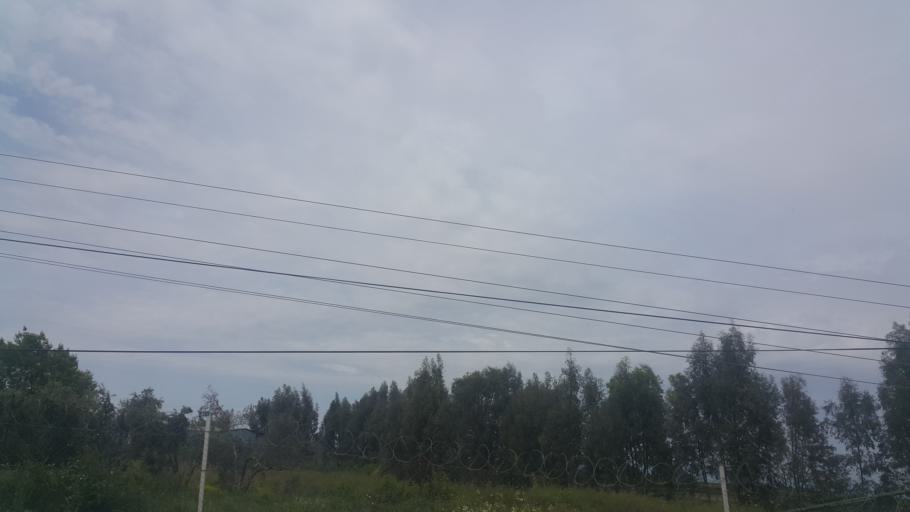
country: TR
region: Adana
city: Ceyhan
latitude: 37.0453
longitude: 35.7649
